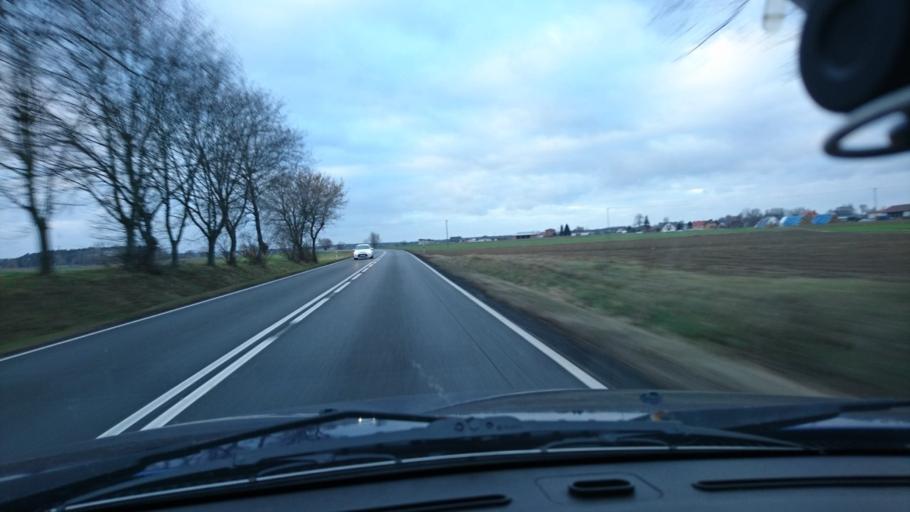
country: PL
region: Greater Poland Voivodeship
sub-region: Powiat kepinski
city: Opatow
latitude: 51.2169
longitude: 18.1397
